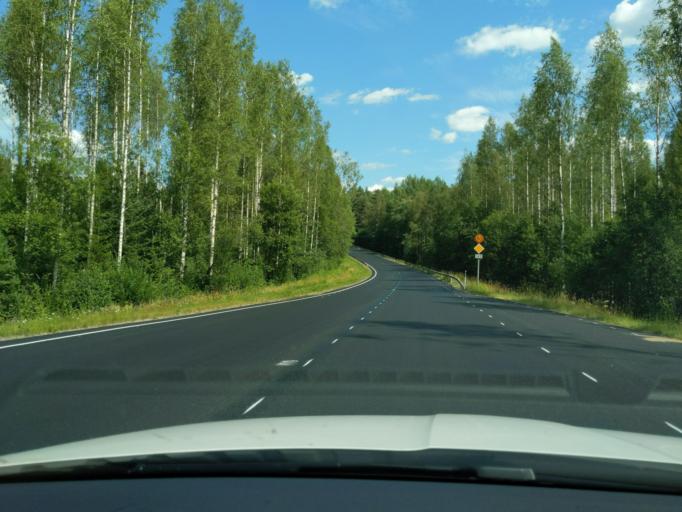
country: FI
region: Paijanne Tavastia
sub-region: Lahti
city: Nastola
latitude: 61.0922
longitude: 25.8880
